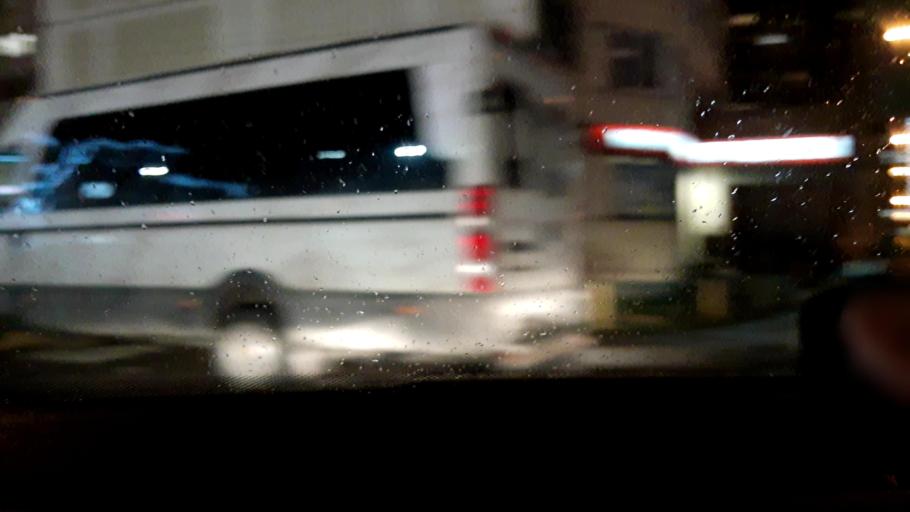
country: RU
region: Moskovskaya
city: Dolgoprudnyy
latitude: 55.9351
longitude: 37.4936
